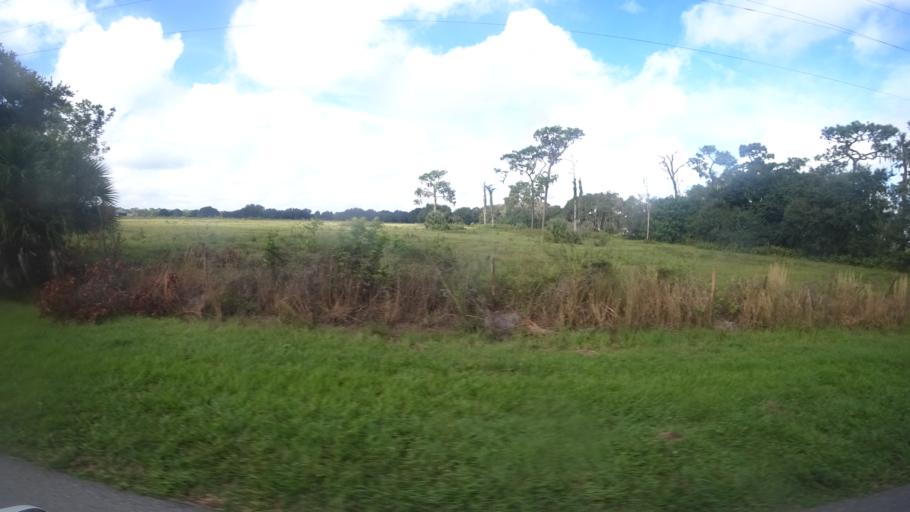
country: US
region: Florida
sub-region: Hillsborough County
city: Sun City Center
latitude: 27.5971
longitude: -82.3864
